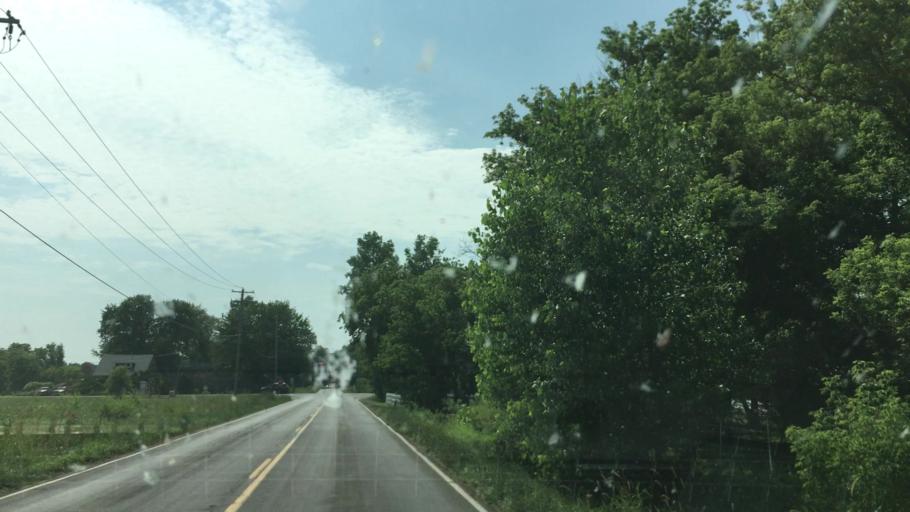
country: US
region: Michigan
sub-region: Kent County
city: Byron Center
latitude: 42.7830
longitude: -85.7209
